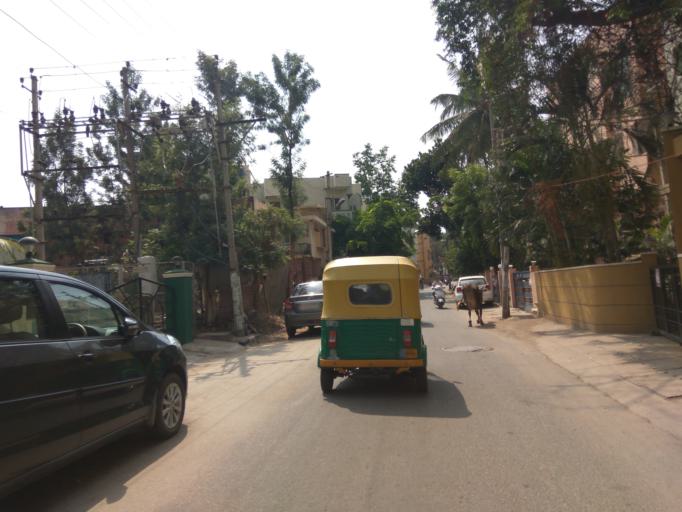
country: IN
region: Karnataka
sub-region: Bangalore Urban
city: Bangalore
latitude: 12.9947
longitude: 77.6245
